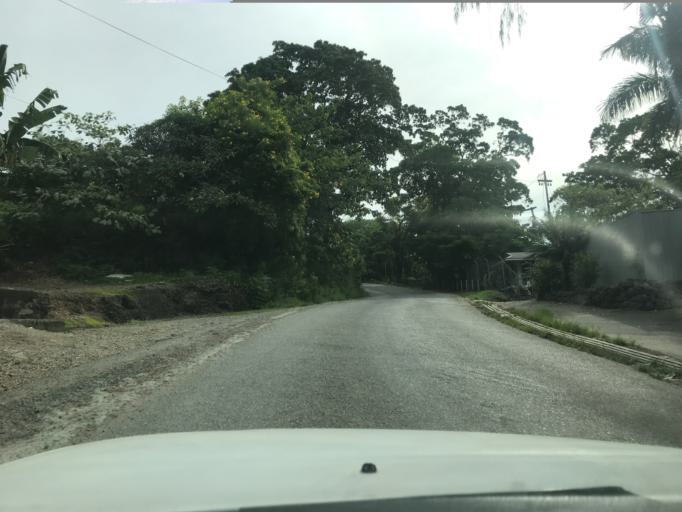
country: SB
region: Guadalcanal
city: Honiara
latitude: -9.4320
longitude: 159.9458
